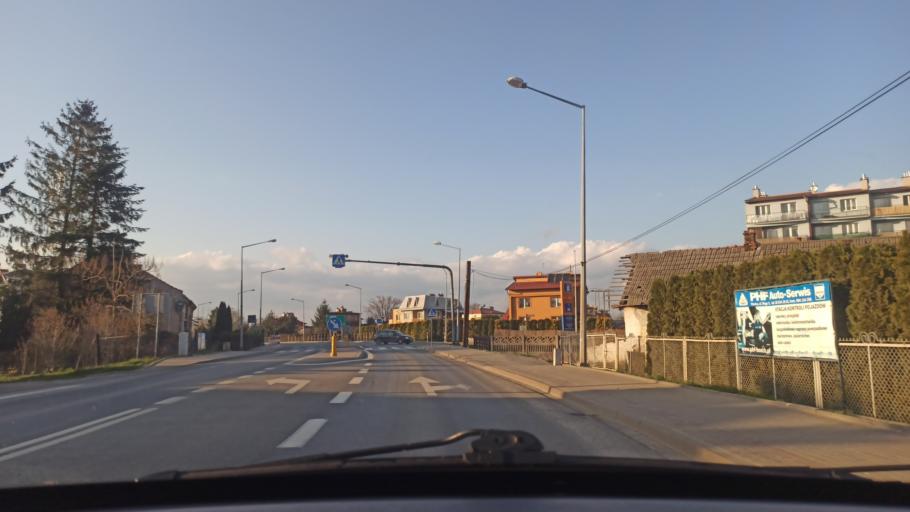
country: PL
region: Subcarpathian Voivodeship
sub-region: Powiat jaroslawski
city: Radymno
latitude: 49.9445
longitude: 22.8245
